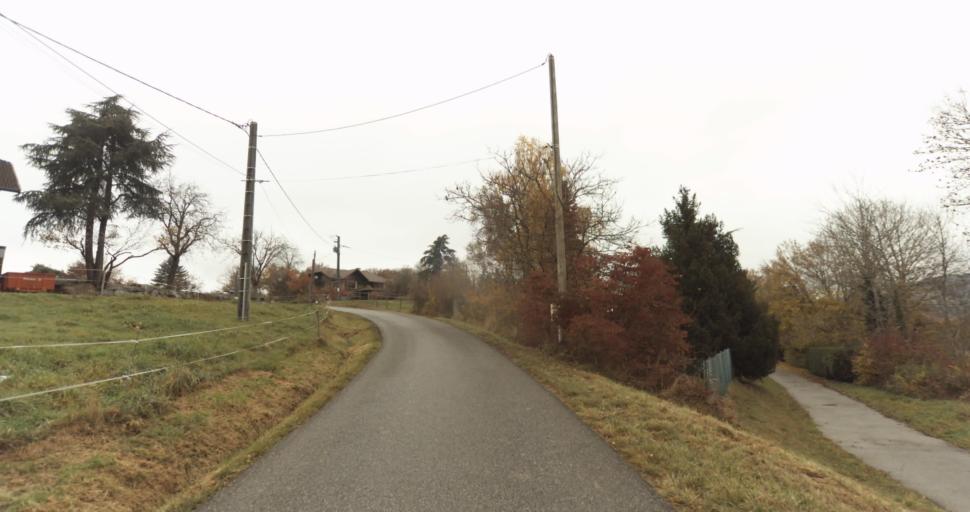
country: FR
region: Rhone-Alpes
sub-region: Departement de la Haute-Savoie
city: Groisy
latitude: 46.0213
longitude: 6.1978
